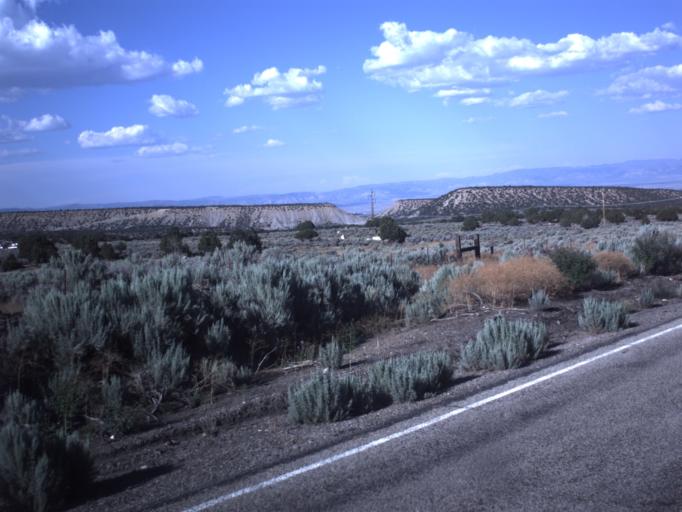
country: US
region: Utah
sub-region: Emery County
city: Huntington
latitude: 39.4841
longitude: -111.0010
